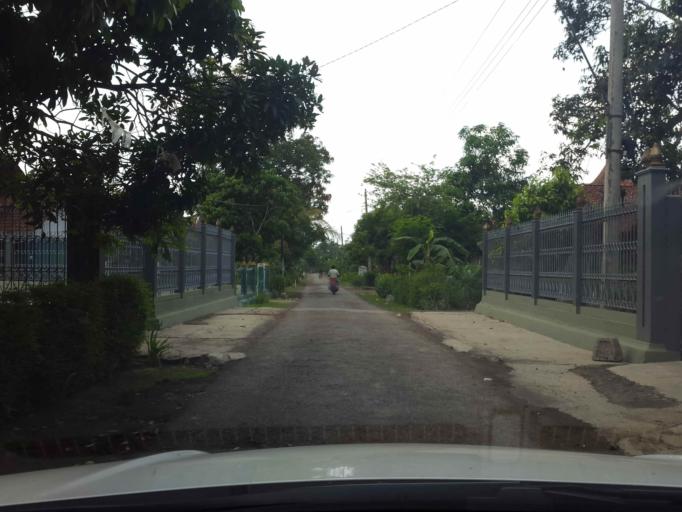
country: ID
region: Central Java
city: Bakung
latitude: -7.3531
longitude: 108.6753
